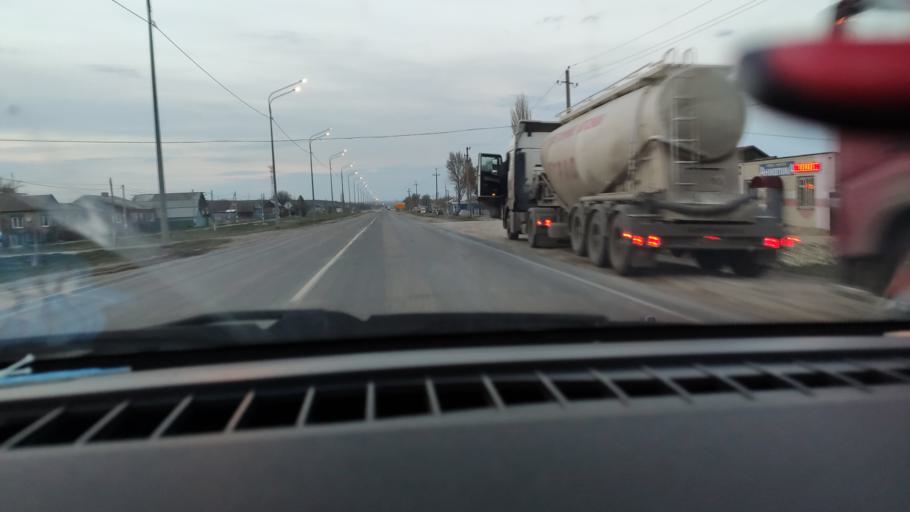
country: RU
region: Saratov
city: Sinodskoye
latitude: 51.9951
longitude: 46.6726
